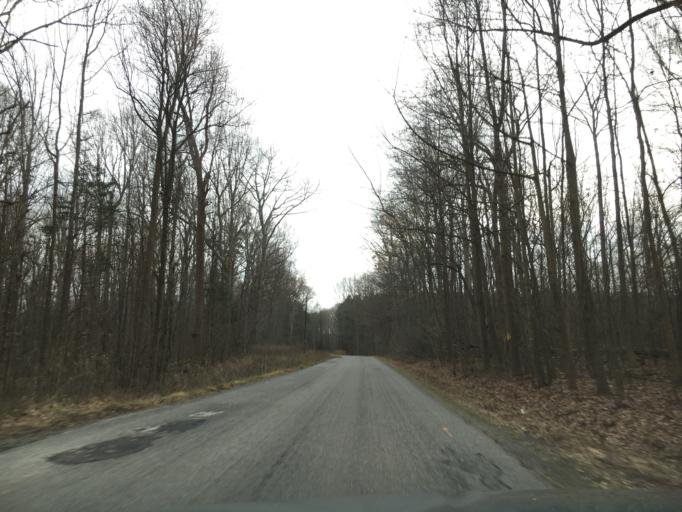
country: US
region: Virginia
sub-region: Amelia County
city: Amelia Court House
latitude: 37.4331
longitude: -78.0172
